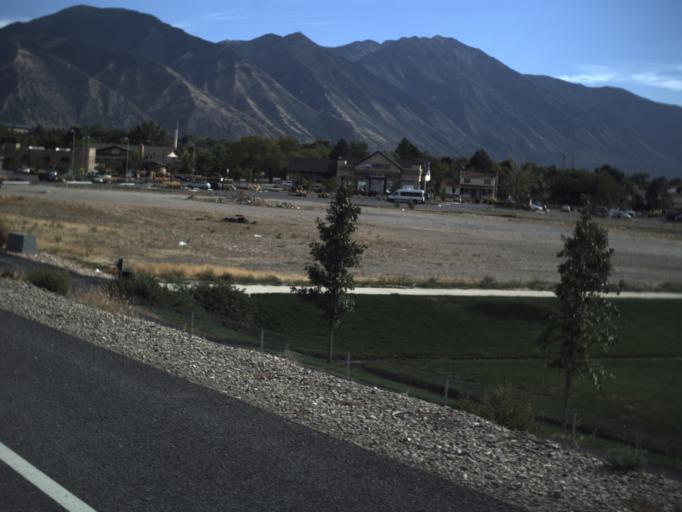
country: US
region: Utah
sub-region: Utah County
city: Spanish Fork
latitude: 40.1257
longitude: -111.6471
